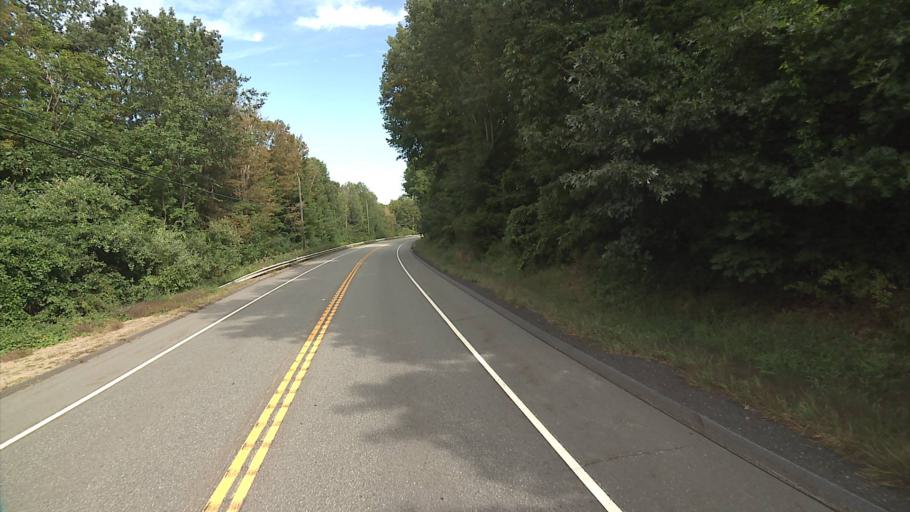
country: US
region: Connecticut
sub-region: Tolland County
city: South Coventry
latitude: 41.8209
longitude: -72.3106
